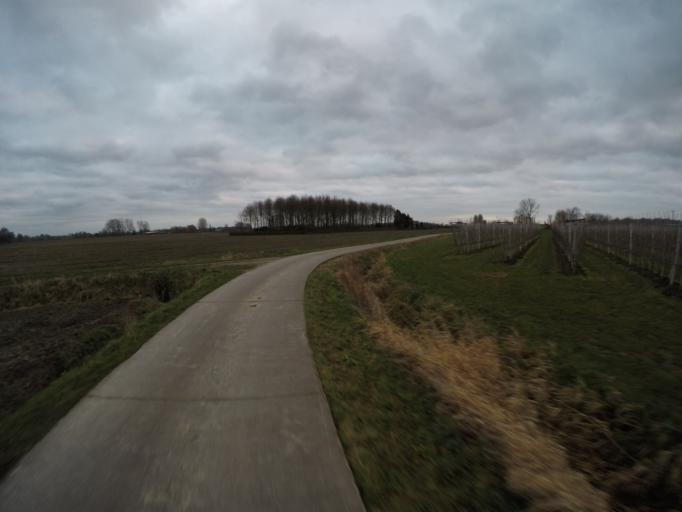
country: BE
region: Flanders
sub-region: Provincie Oost-Vlaanderen
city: Sint-Gillis-Waas
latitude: 51.2250
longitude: 4.1727
